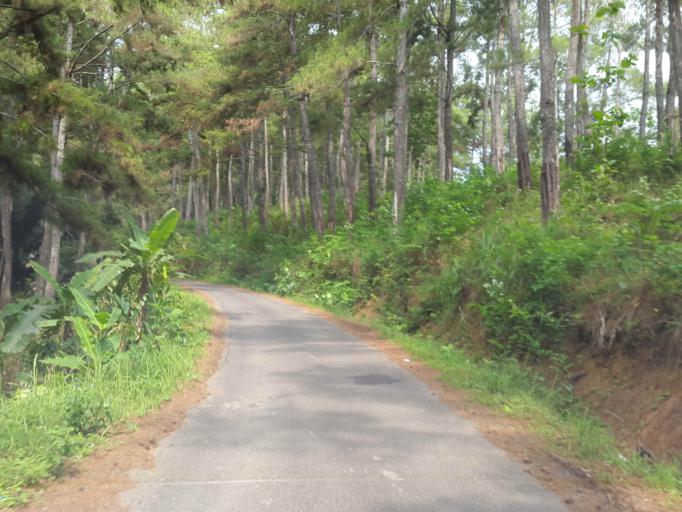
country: ID
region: Central Java
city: Genteng Wetan
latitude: -7.3558
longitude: 108.9103
